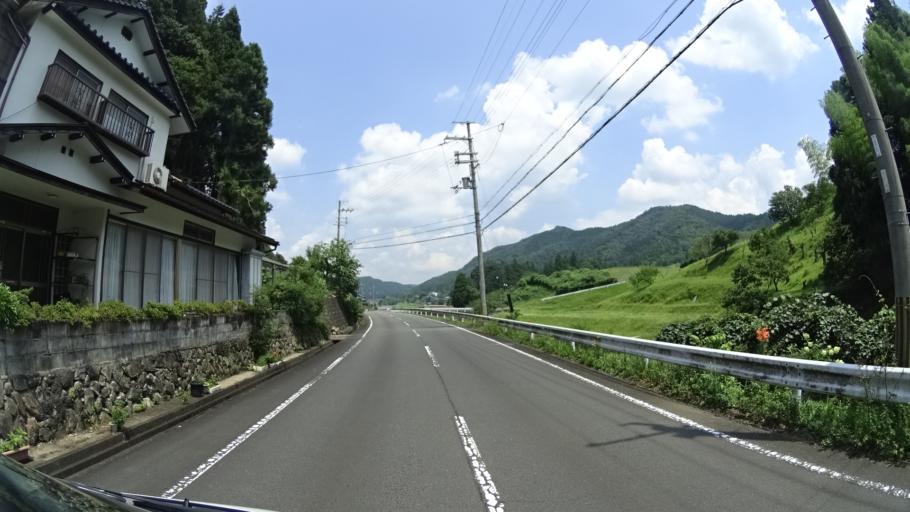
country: JP
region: Kyoto
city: Ayabe
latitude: 35.1973
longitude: 135.2199
